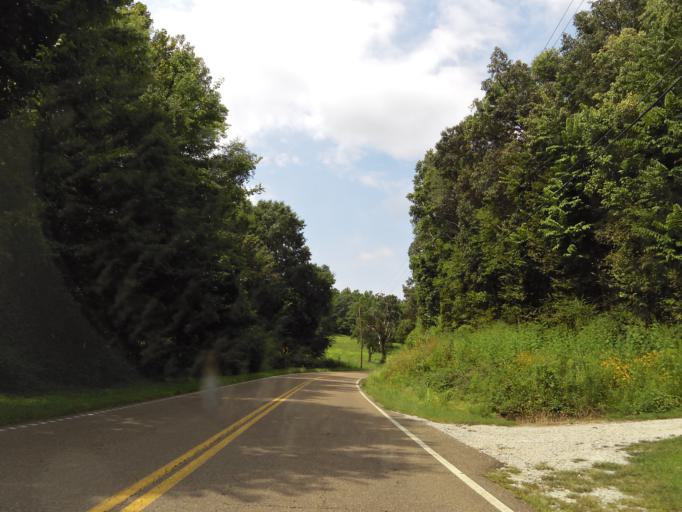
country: US
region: Tennessee
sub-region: Decatur County
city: Decaturville
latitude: 35.5810
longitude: -88.0746
